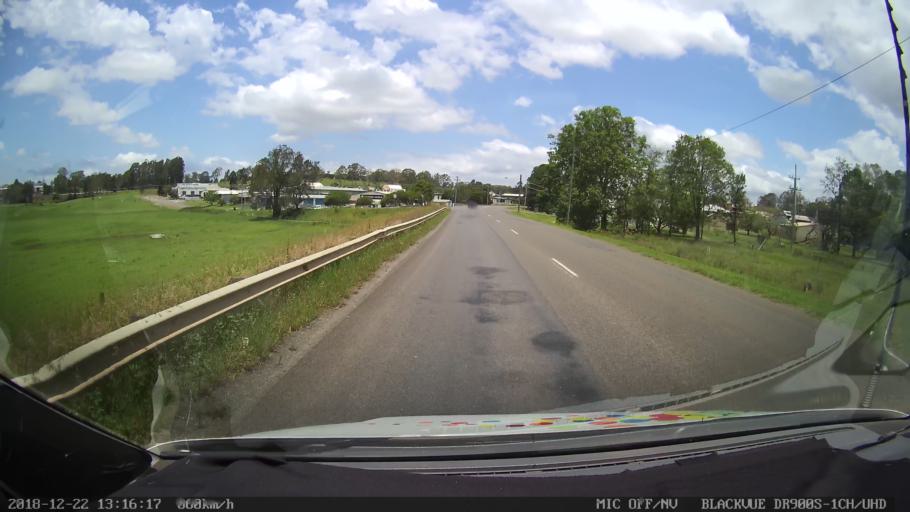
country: AU
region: New South Wales
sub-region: Clarence Valley
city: South Grafton
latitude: -29.7249
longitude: 152.9390
